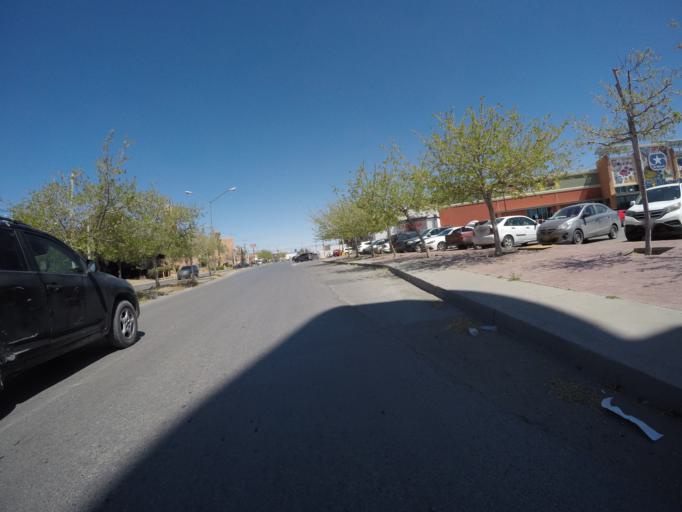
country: MX
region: Chihuahua
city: Ciudad Juarez
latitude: 31.7010
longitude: -106.4137
